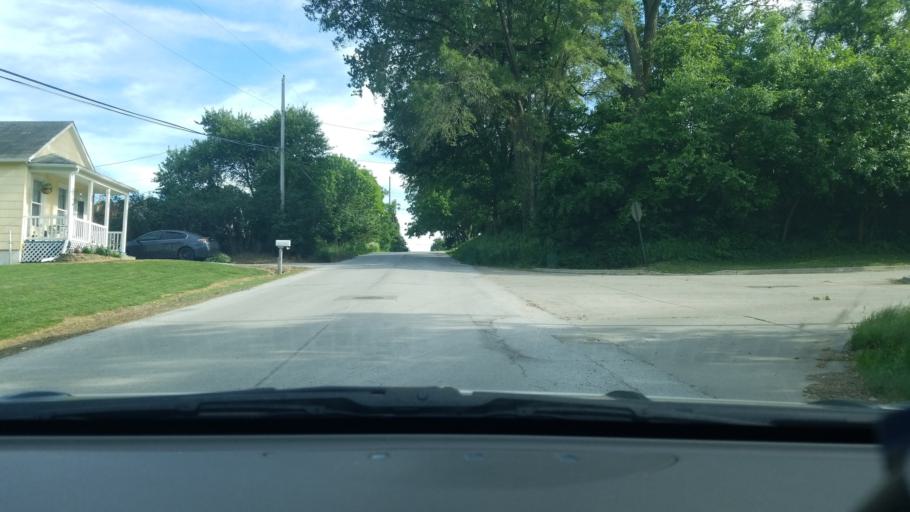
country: US
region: Nebraska
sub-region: Sarpy County
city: Offutt Air Force Base
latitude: 41.1713
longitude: -95.9335
